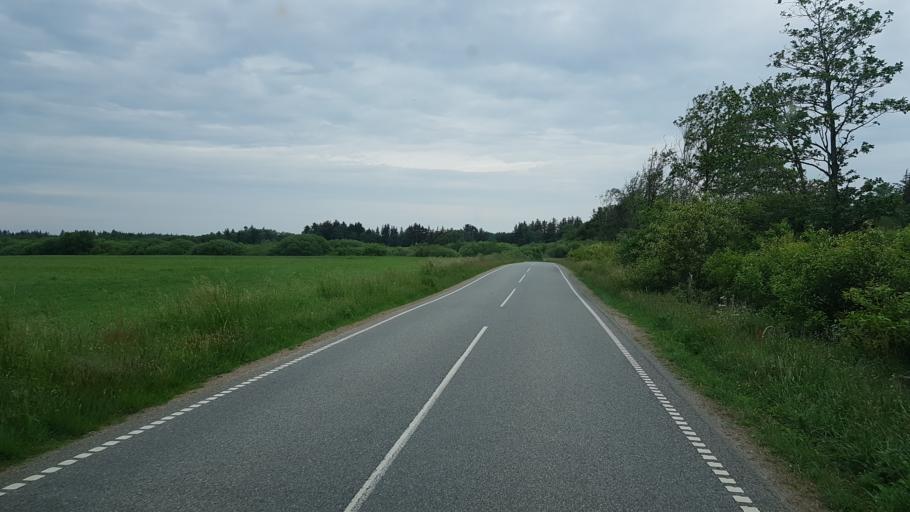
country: DK
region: South Denmark
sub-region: Varde Kommune
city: Oksbol
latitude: 55.6785
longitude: 8.3114
